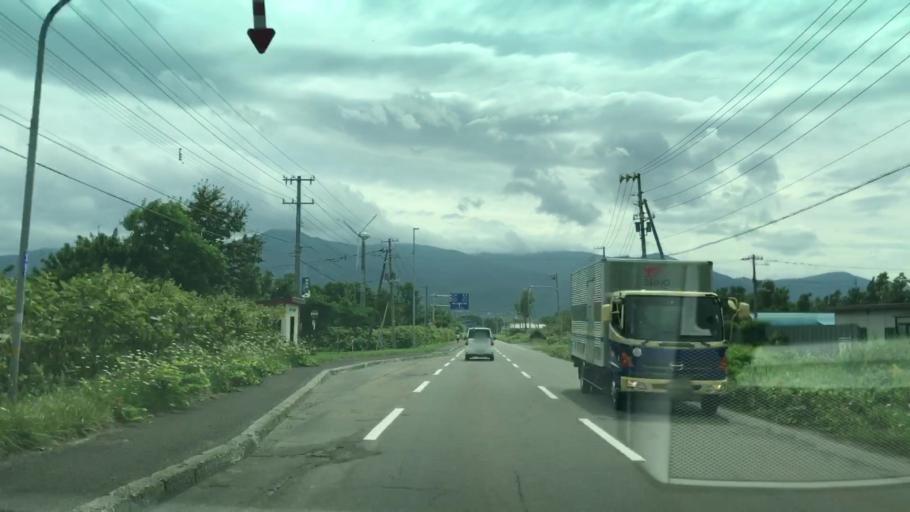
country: JP
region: Hokkaido
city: Iwanai
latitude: 43.0021
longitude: 140.5409
